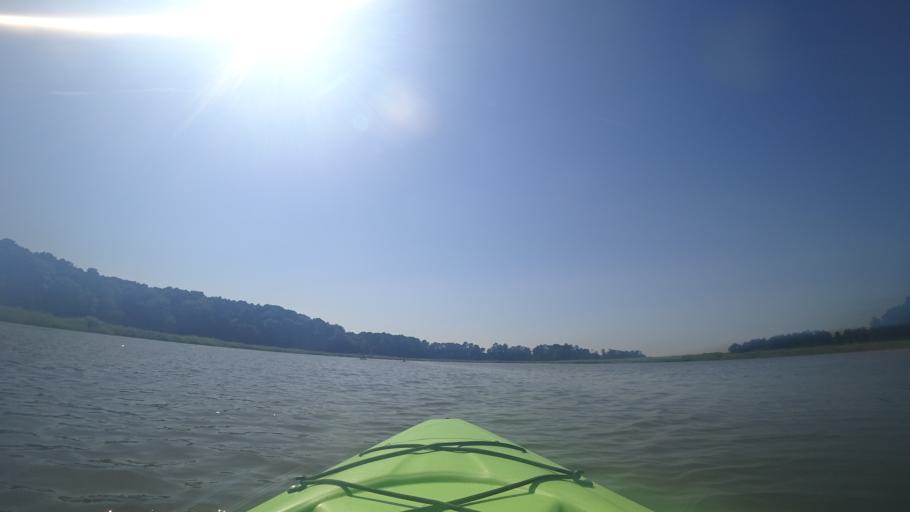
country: US
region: Virginia
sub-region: Isle of Wight County
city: Smithfield
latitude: 36.9692
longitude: -76.6163
